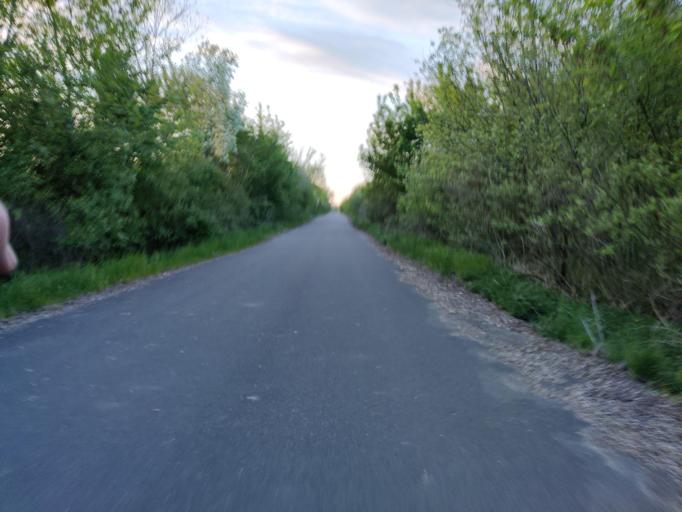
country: DE
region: Saxony
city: Bohlen
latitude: 51.2325
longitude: 12.3681
